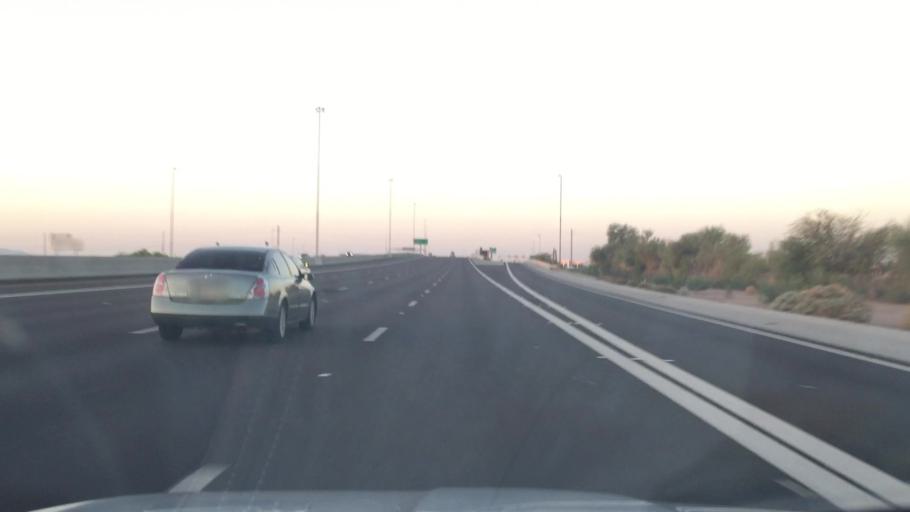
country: US
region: Arizona
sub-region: Maricopa County
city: Scottsdale
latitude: 33.5011
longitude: -111.8890
